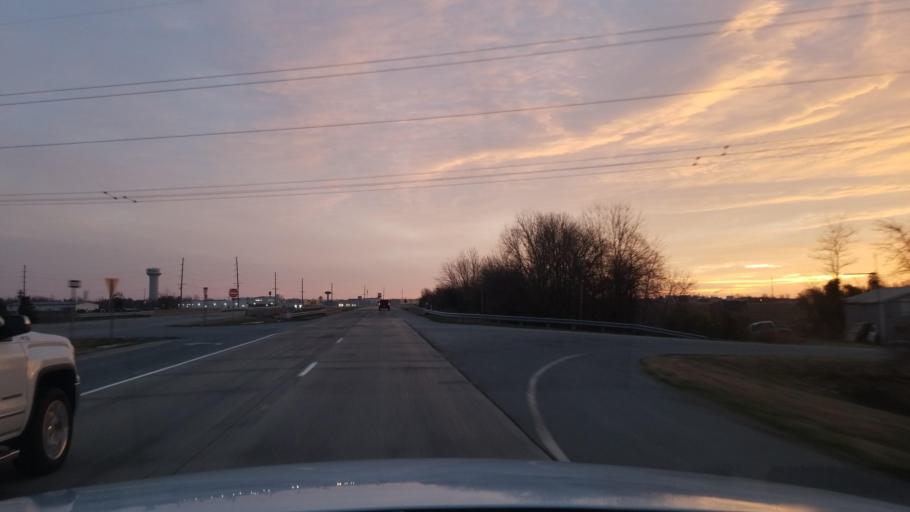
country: US
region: Indiana
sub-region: Posey County
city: Mount Vernon
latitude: 37.9411
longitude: -87.8606
